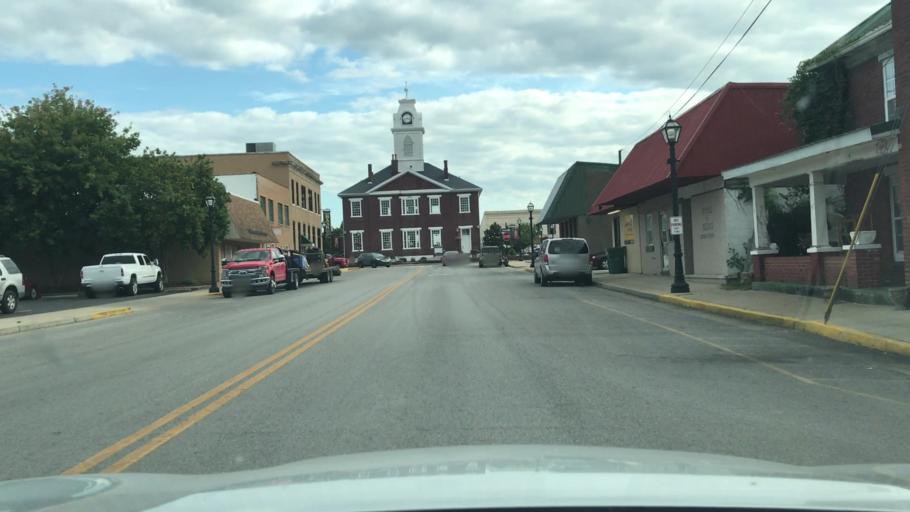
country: US
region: Kentucky
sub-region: Todd County
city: Elkton
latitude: 36.8084
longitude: -87.1544
